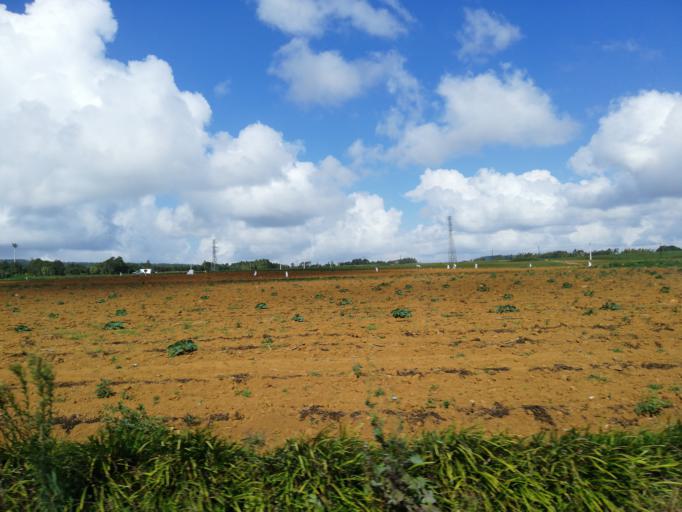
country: MU
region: Pamplemousses
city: Creve Coeur
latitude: -20.2092
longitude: 57.5573
